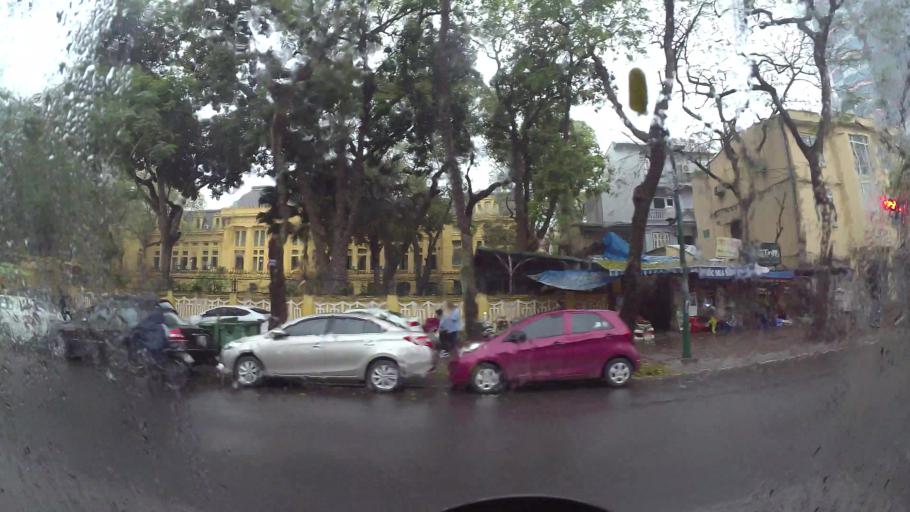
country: VN
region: Ha Noi
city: Hoan Kiem
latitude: 21.0243
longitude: 105.8472
